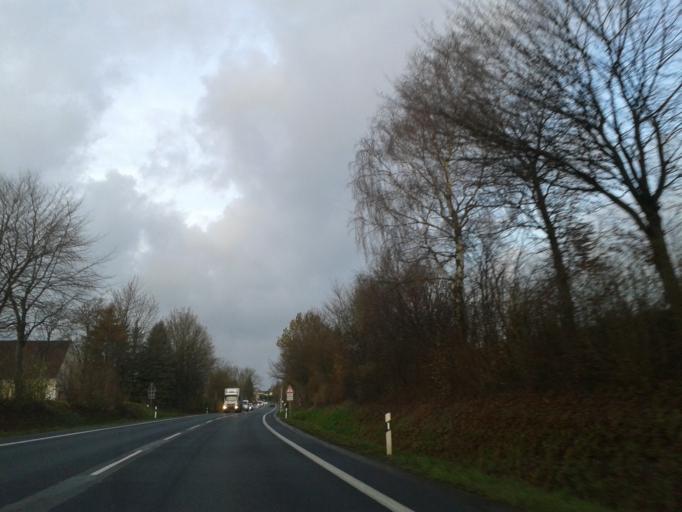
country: DE
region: North Rhine-Westphalia
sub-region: Regierungsbezirk Detmold
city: Blomberg
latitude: 51.9437
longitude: 9.0682
